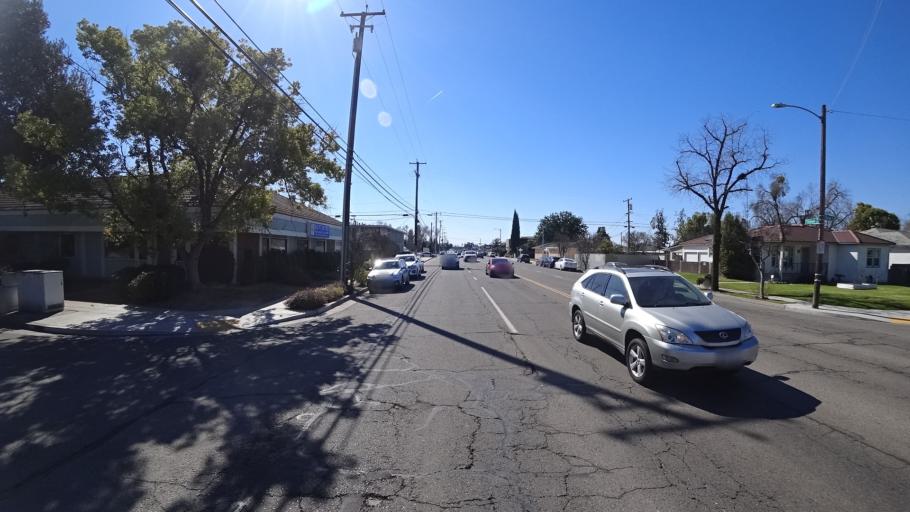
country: US
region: California
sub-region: Fresno County
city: Fresno
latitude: 36.7751
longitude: -119.7815
